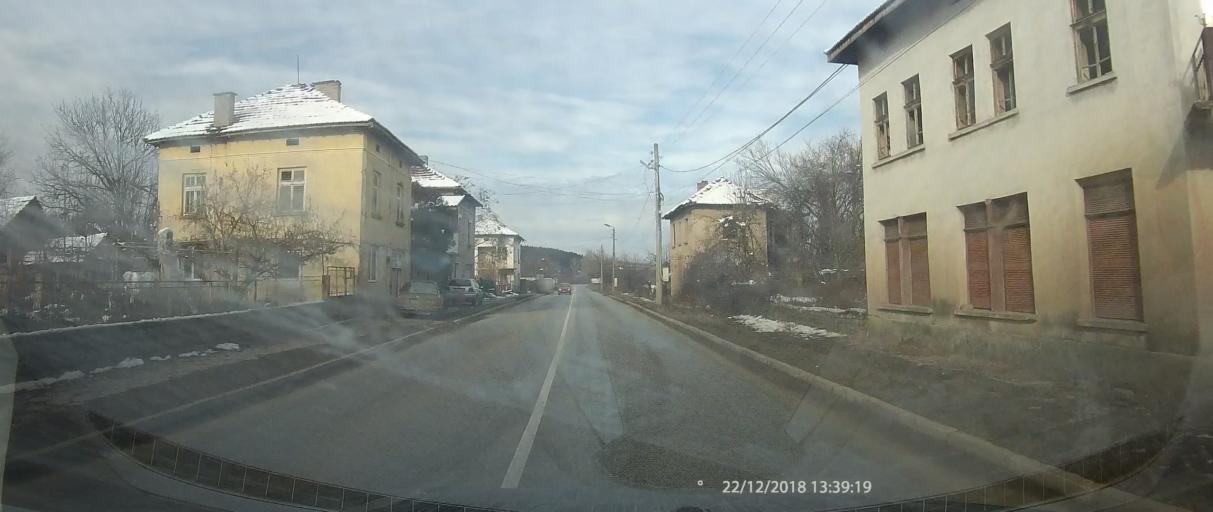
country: BG
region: Lovech
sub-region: Obshtina Lukovit
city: Lukovit
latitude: 43.1613
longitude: 24.1483
